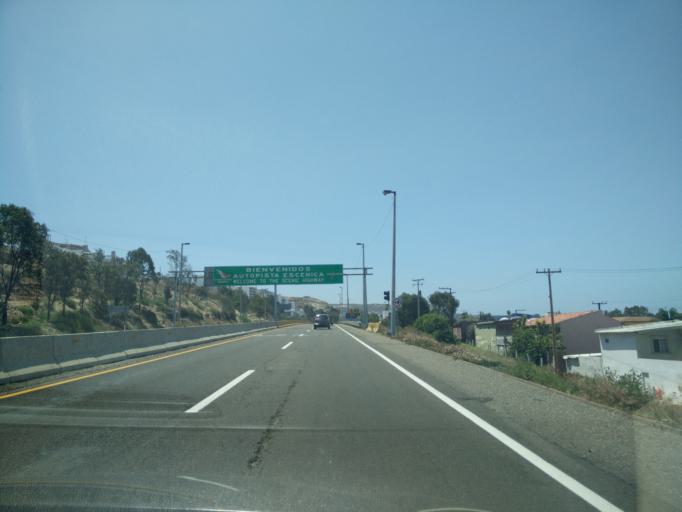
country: US
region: California
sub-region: San Diego County
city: Imperial Beach
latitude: 32.5296
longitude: -117.1085
